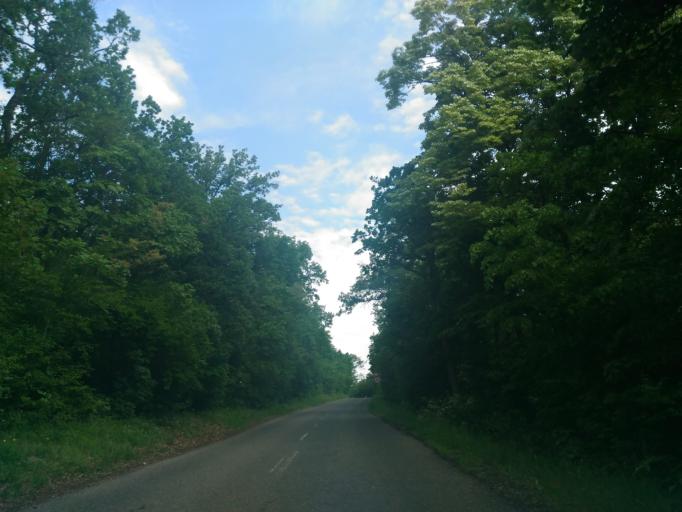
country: HU
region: Baranya
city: Pecs
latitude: 46.0985
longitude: 18.2272
